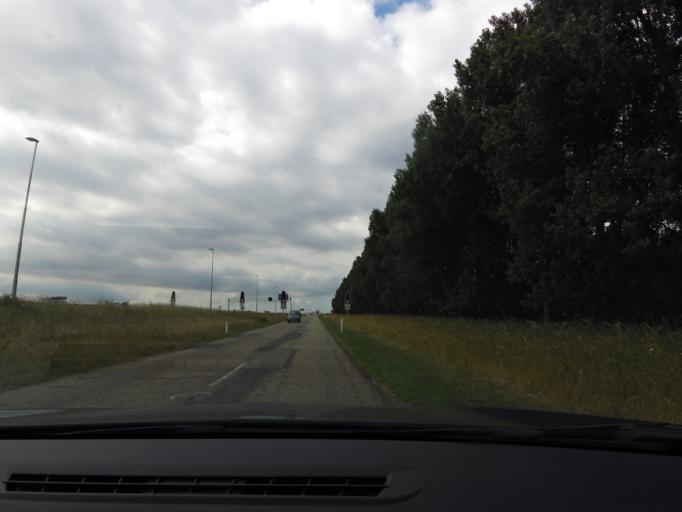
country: NL
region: North Brabant
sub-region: Gemeente Moerdijk
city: Willemstad
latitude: 51.6858
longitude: 4.4125
